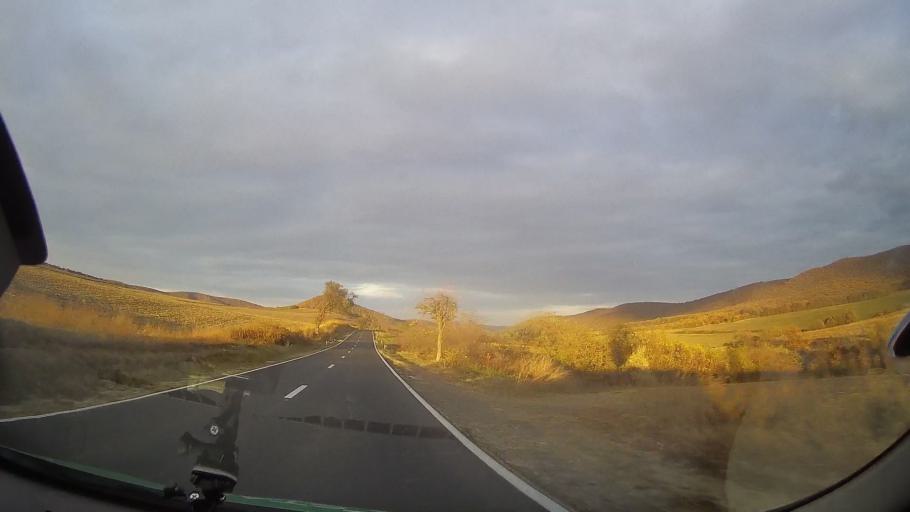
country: RO
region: Tulcea
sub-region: Comuna Ciucurova
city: Ciucurova
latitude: 44.9377
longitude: 28.4907
